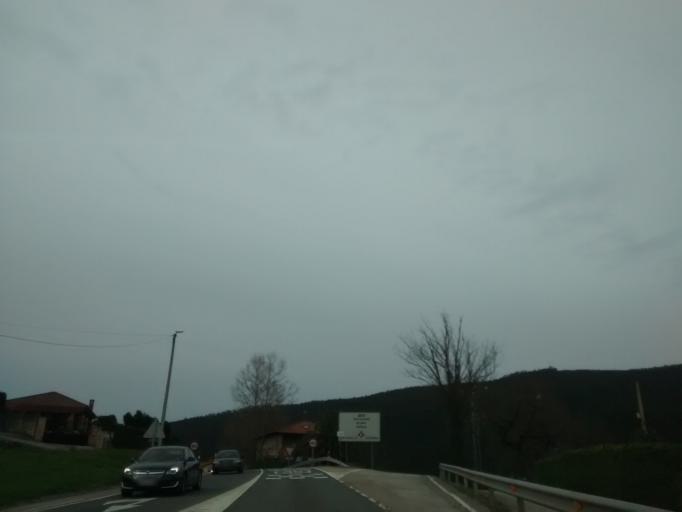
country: ES
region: Cantabria
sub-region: Provincia de Cantabria
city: Puente Viesgo
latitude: 43.3200
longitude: -3.9622
